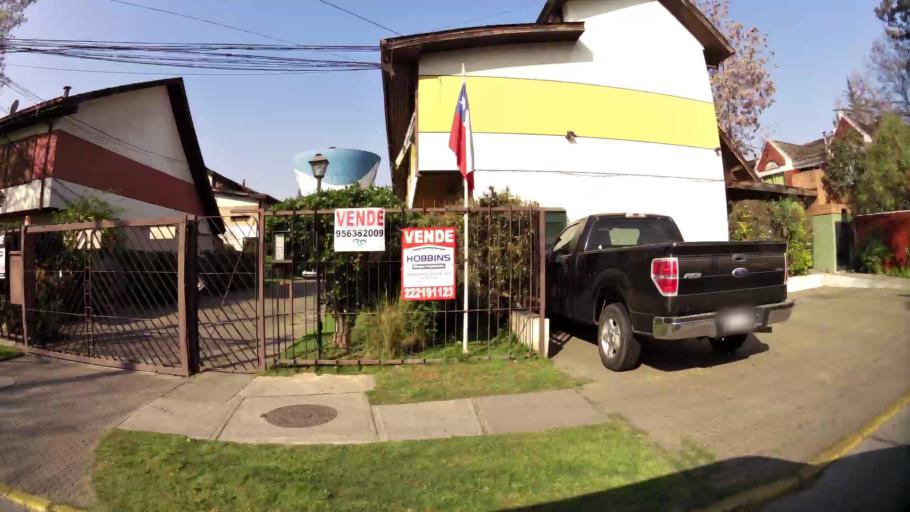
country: CL
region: Santiago Metropolitan
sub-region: Provincia de Santiago
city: Villa Presidente Frei, Nunoa, Santiago, Chile
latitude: -33.3787
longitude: -70.5432
